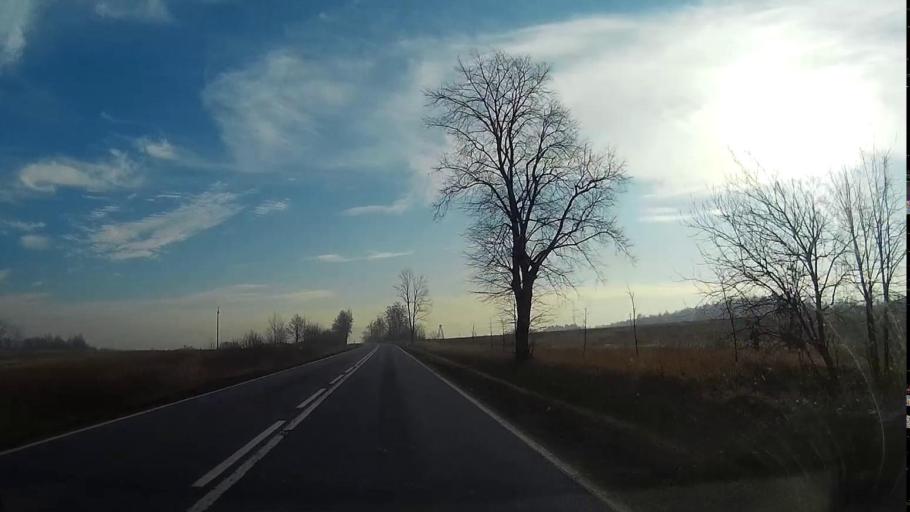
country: PL
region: Lesser Poland Voivodeship
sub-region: Powiat chrzanowski
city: Kwaczala
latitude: 50.0616
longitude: 19.5022
